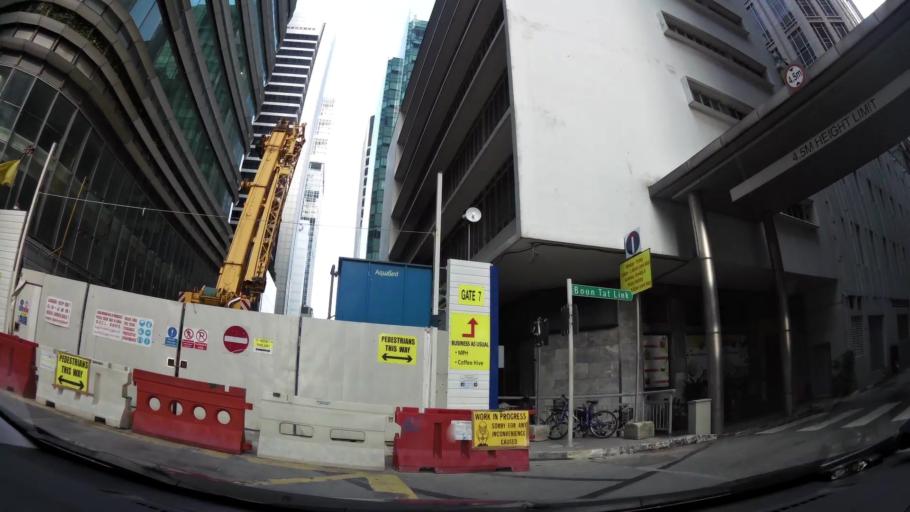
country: SG
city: Singapore
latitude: 1.2785
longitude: 103.8492
